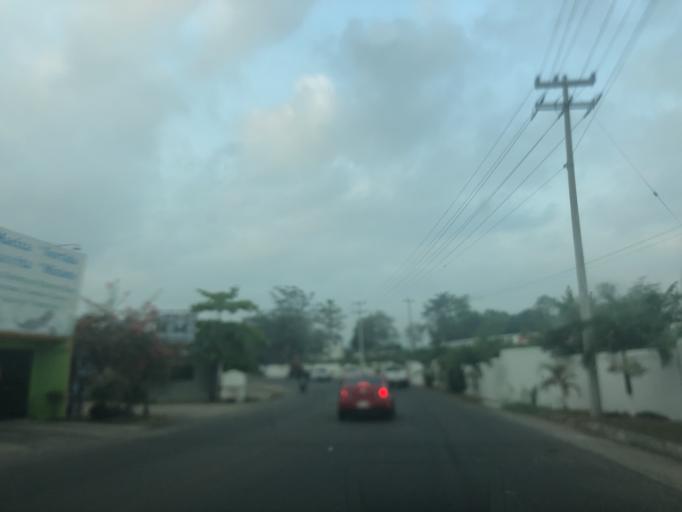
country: MX
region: Chiapas
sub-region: Reforma
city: El Carmen (El Limon)
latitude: 17.8715
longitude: -93.1529
